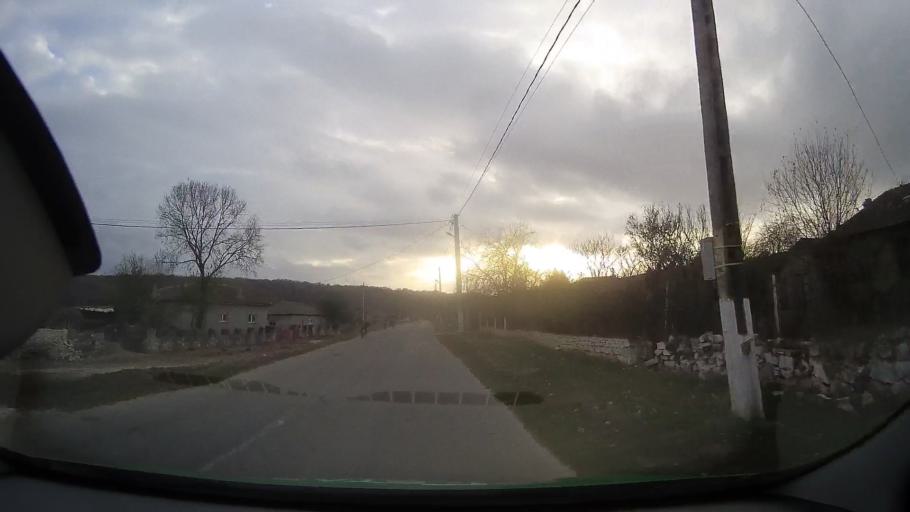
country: RO
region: Constanta
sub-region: Comuna Adamclisi
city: Adamclisi
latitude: 44.0424
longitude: 27.9552
